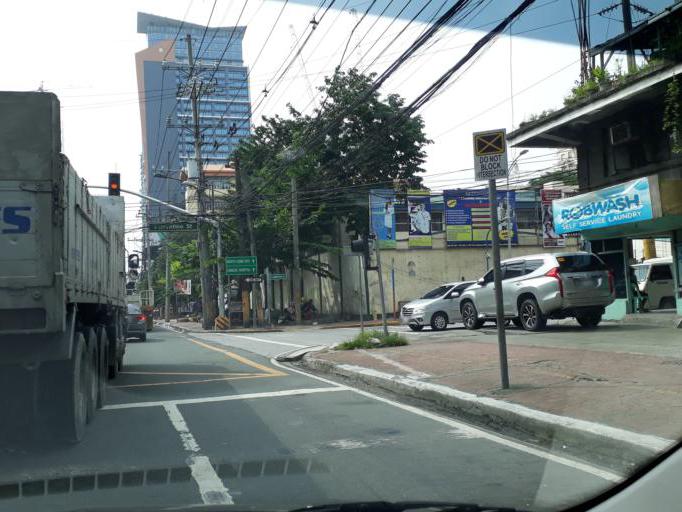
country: PH
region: Metro Manila
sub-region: City of Manila
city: Manila
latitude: 14.6106
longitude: 120.9918
